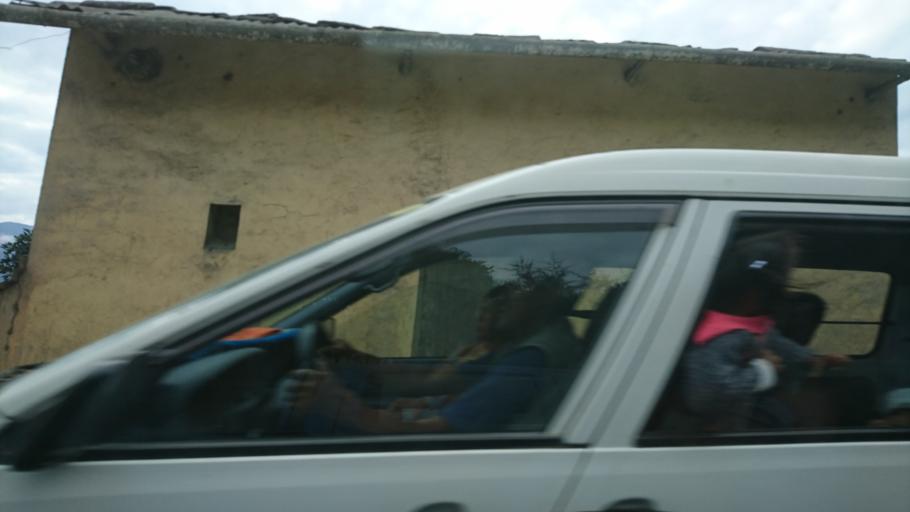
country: BO
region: La Paz
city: Coroico
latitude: -16.1953
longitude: -67.7093
